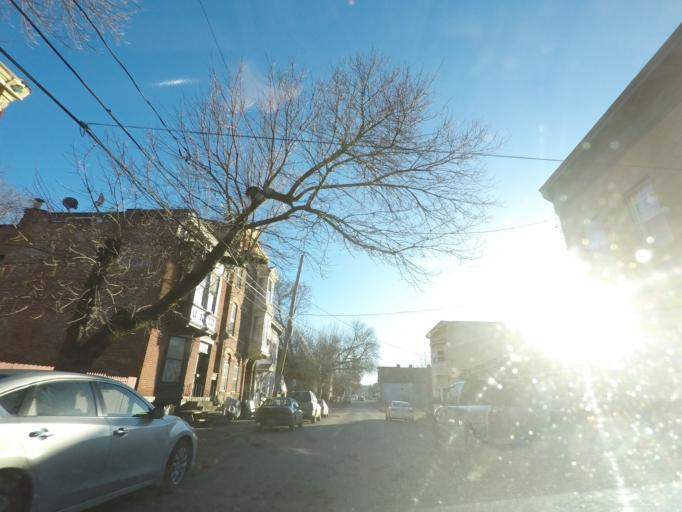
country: US
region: New York
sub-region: Albany County
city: Green Island
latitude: 42.7412
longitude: -73.6812
